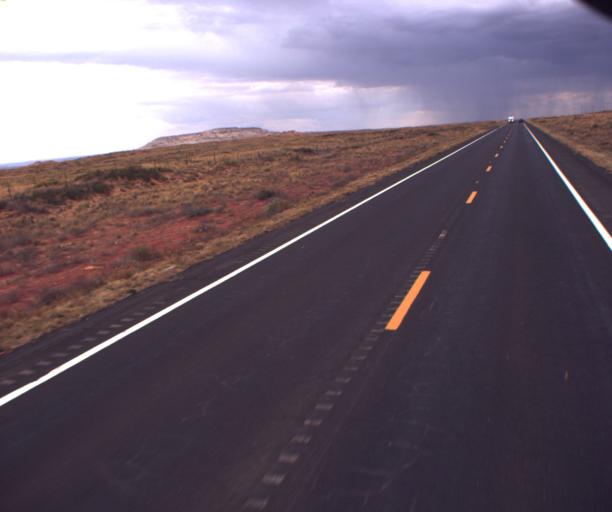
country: US
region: Arizona
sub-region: Coconino County
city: Tuba City
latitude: 36.2848
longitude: -110.9987
